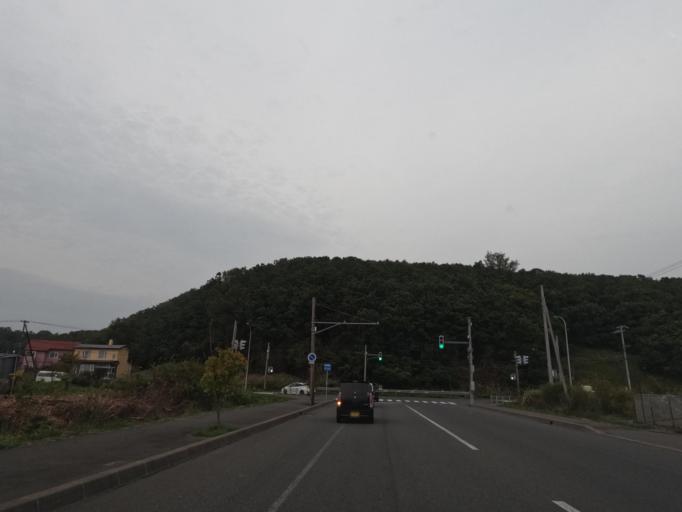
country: JP
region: Hokkaido
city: Date
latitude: 42.3833
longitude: 140.9118
